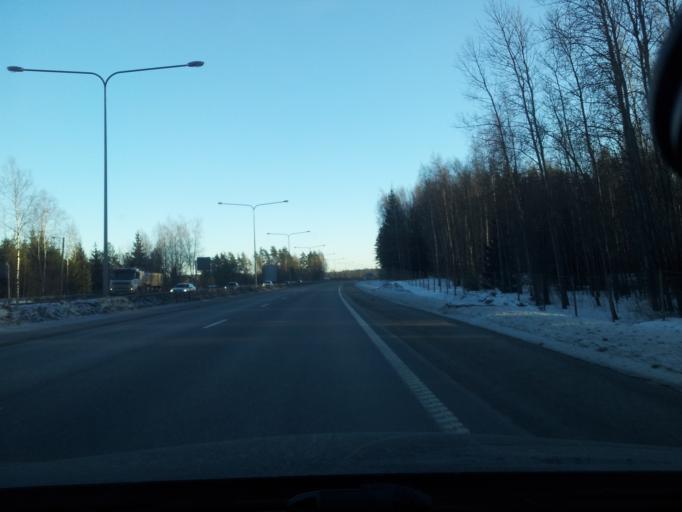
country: FI
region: Uusimaa
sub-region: Helsinki
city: Espoo
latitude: 60.2422
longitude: 24.5725
